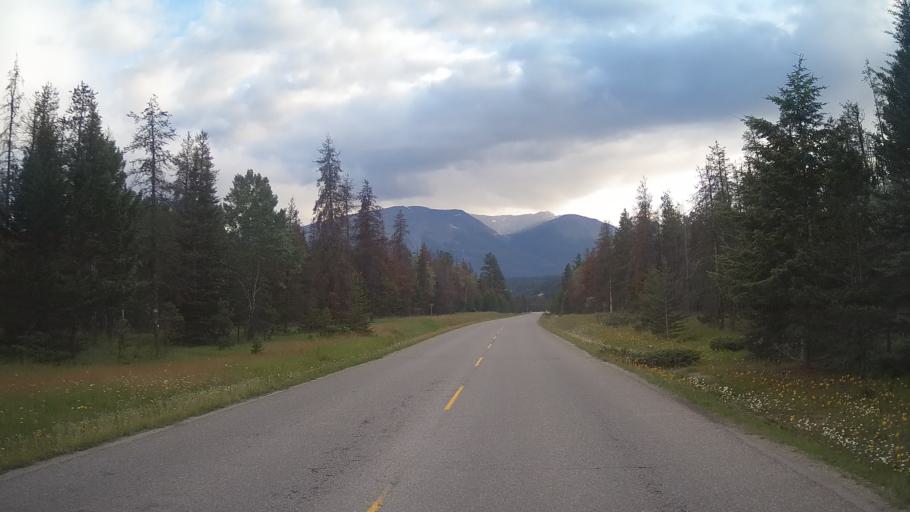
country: CA
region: Alberta
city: Jasper Park Lodge
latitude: 52.9147
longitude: -118.0481
